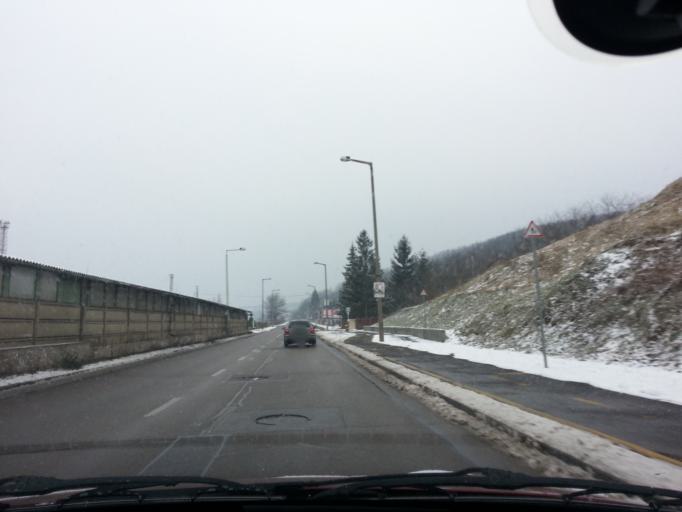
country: HU
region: Nograd
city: Salgotarjan
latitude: 48.0951
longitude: 19.7956
